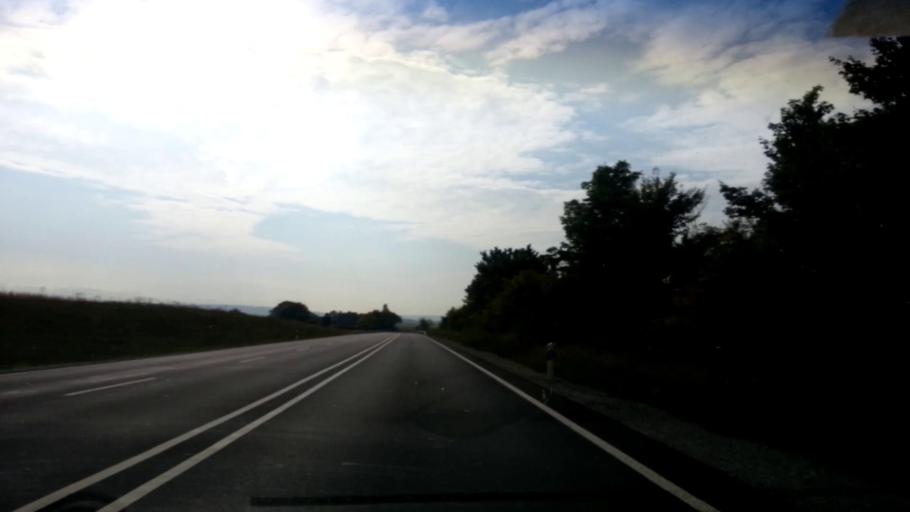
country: DE
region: Bavaria
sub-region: Regierungsbezirk Unterfranken
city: Gerolzhofen
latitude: 49.8789
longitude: 10.3584
